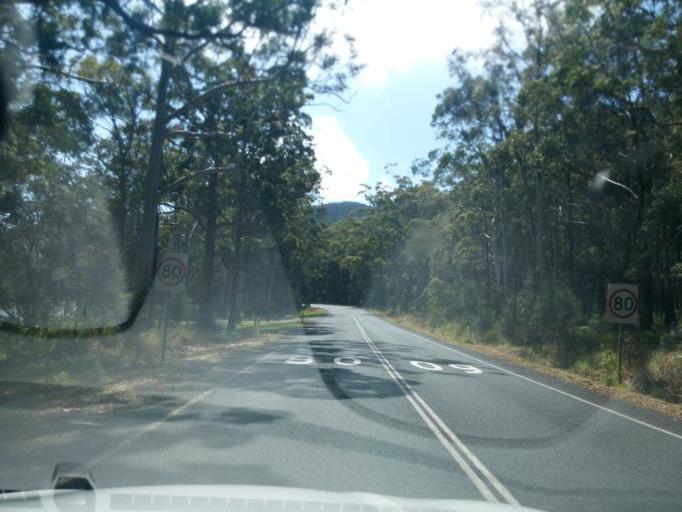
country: AU
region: New South Wales
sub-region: Great Lakes
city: Forster
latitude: -32.3270
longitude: 152.5276
